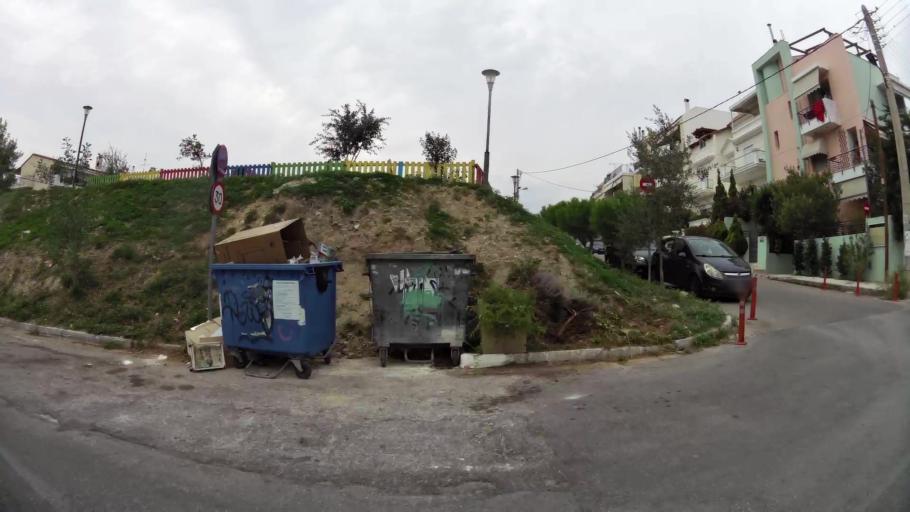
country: GR
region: Attica
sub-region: Nomarchia Athinas
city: Alimos
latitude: 37.9177
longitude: 23.7271
